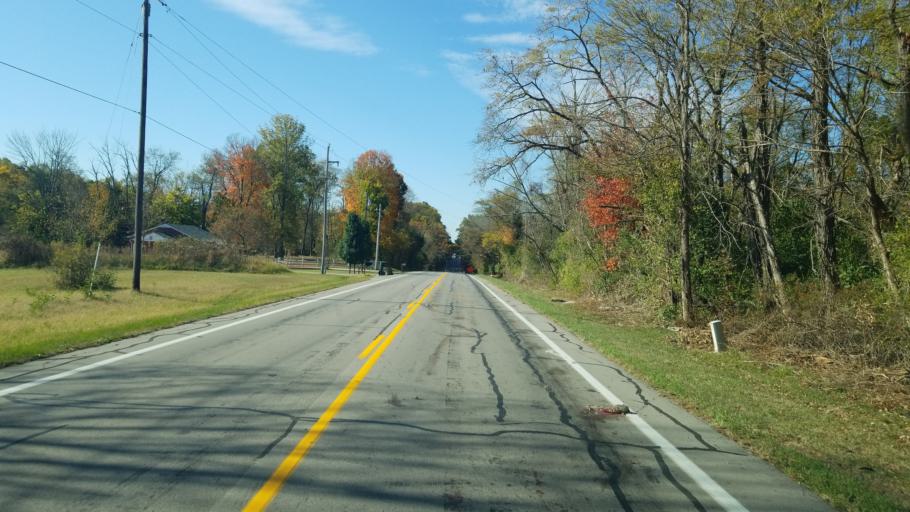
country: US
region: Ohio
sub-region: Warren County
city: Morrow
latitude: 39.3784
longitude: -84.0492
